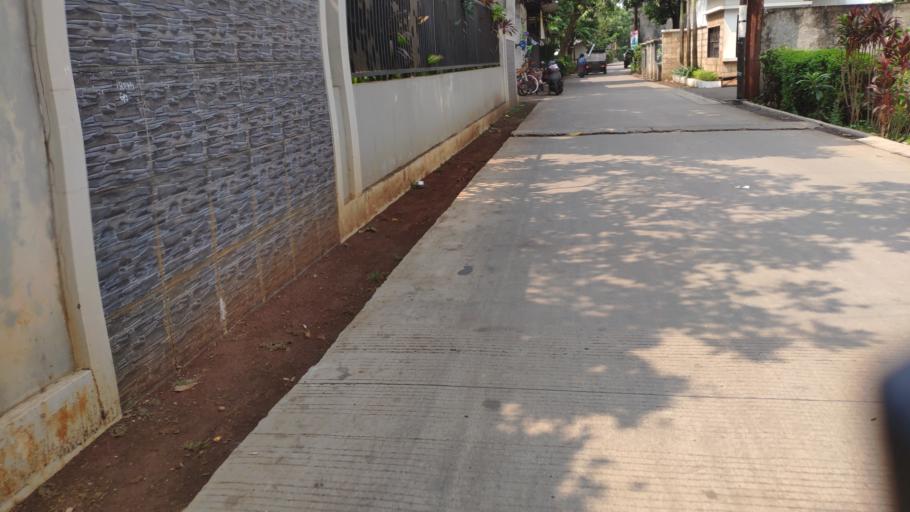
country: ID
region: West Java
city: Depok
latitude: -6.3130
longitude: 106.8308
